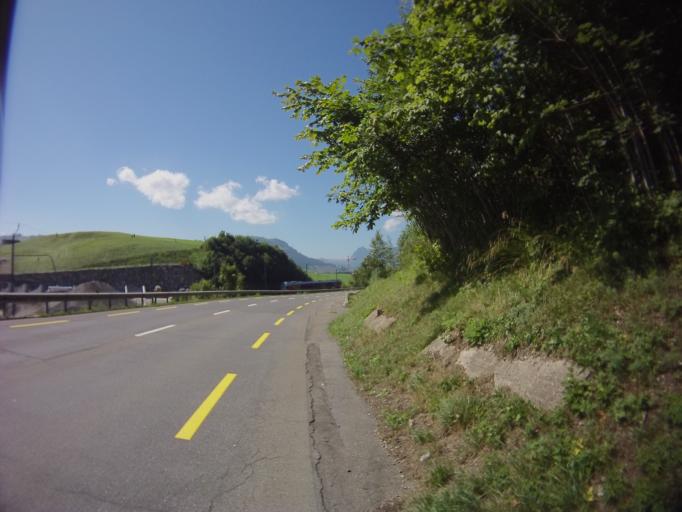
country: CH
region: Schwyz
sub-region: Bezirk Einsiedeln
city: Einsiedeln
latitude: 47.1421
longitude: 8.7498
